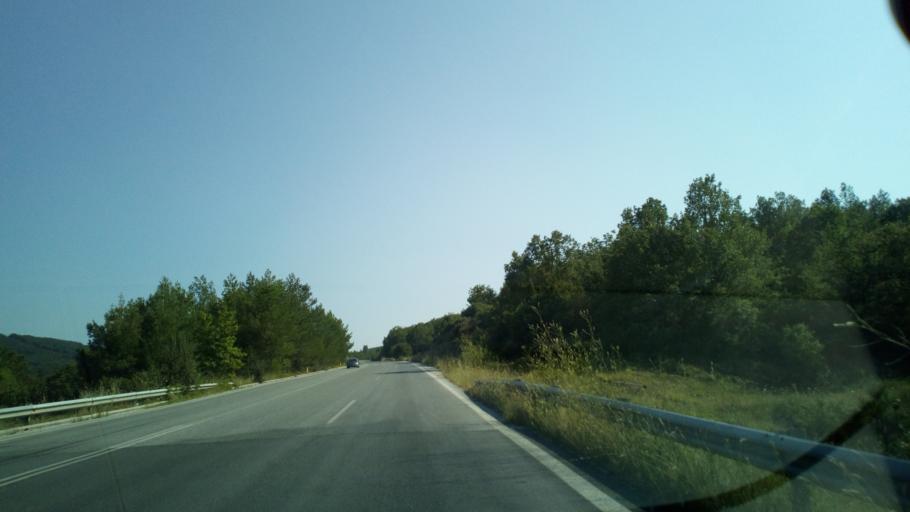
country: GR
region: Central Macedonia
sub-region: Nomos Chalkidikis
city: Polygyros
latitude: 40.4138
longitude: 23.4213
